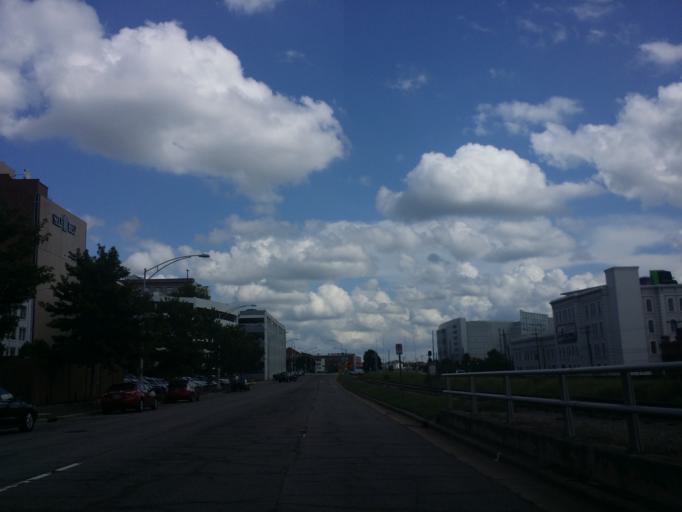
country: US
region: North Carolina
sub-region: Durham County
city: Durham
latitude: 35.9961
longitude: -78.9042
